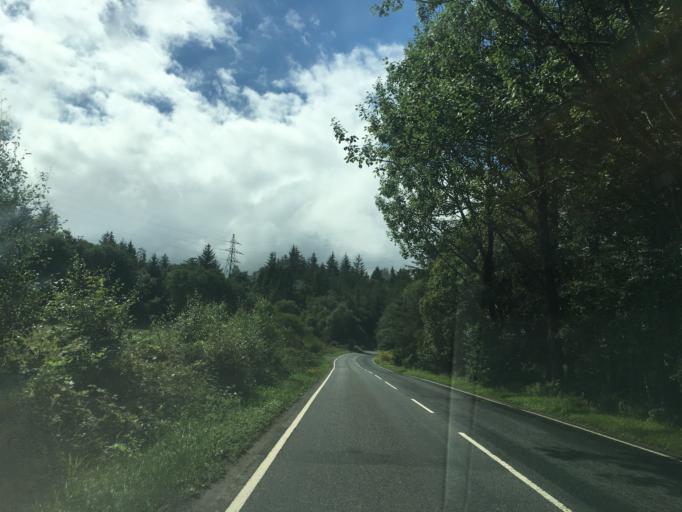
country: GB
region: Scotland
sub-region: Argyll and Bute
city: Dunoon
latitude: 55.9949
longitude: -4.9790
